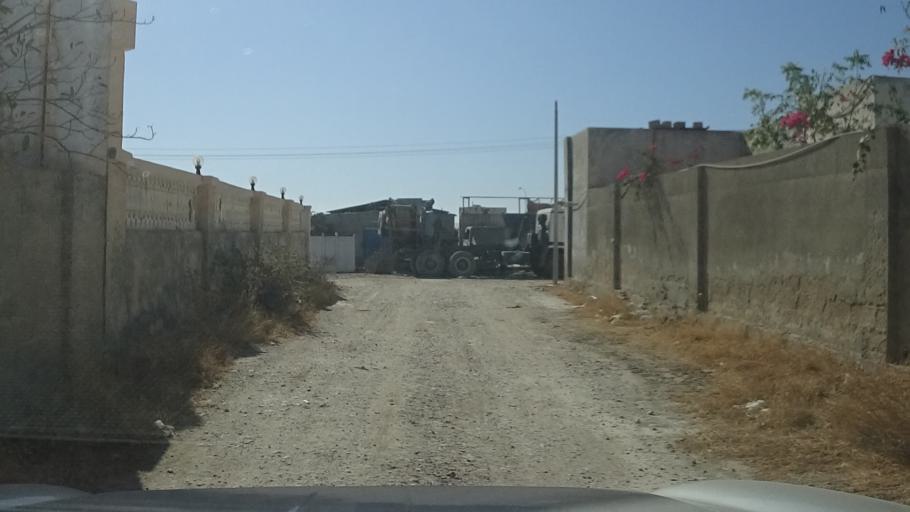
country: OM
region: Zufar
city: Salalah
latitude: 17.0299
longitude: 54.0437
